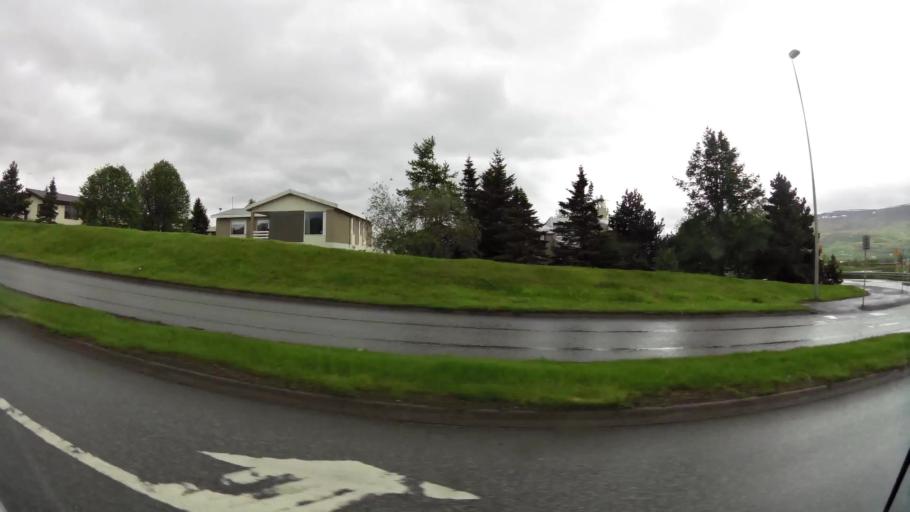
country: IS
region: Northeast
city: Akureyri
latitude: 65.6872
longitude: -18.1248
